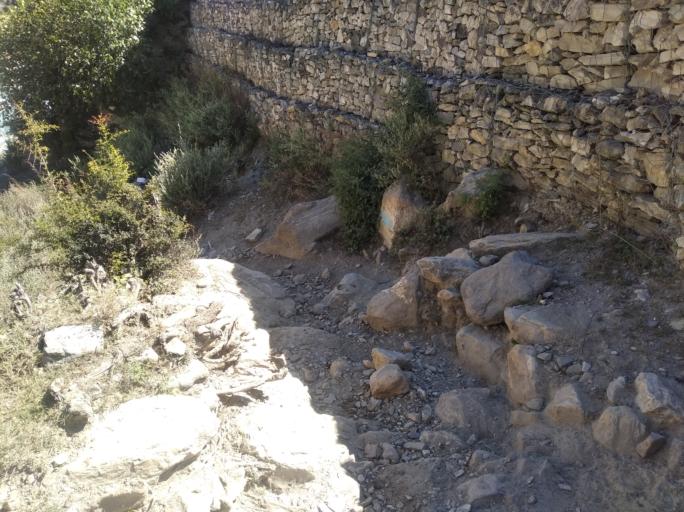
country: NP
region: Mid Western
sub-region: Karnali Zone
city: Jumla
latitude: 28.9374
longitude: 82.9041
